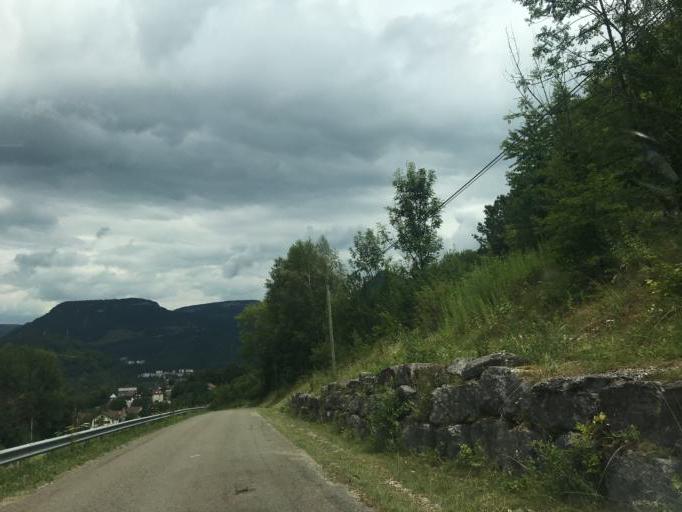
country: FR
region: Franche-Comte
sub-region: Departement du Jura
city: Saint-Claude
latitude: 46.3554
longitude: 5.8577
